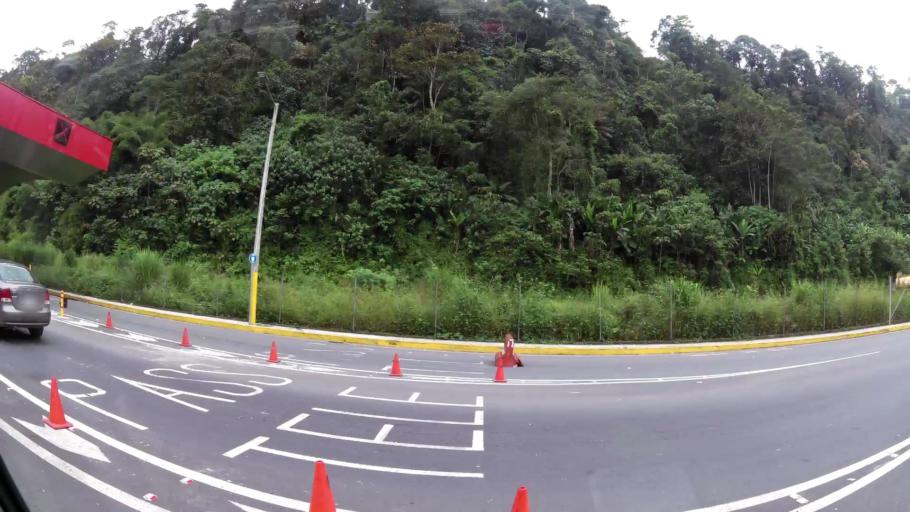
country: EC
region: Santo Domingo de los Tsachilas
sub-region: Canton Santo Domingo de los Colorados
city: Santo Domingo de los Colorados
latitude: -0.2754
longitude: -79.0782
